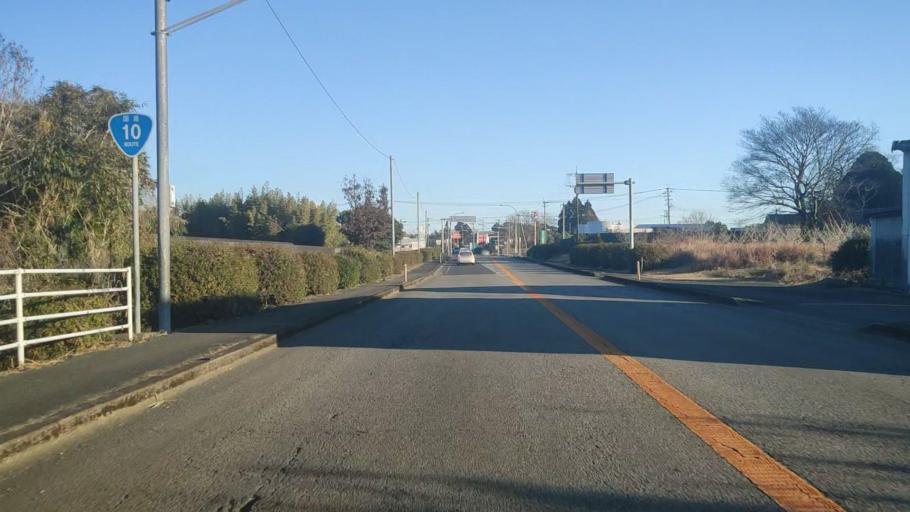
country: JP
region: Miyazaki
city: Takanabe
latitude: 32.1857
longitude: 131.5231
